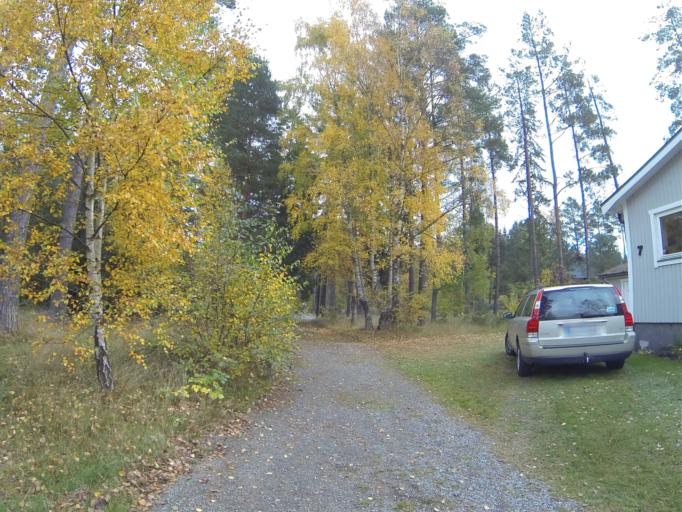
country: SE
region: Skane
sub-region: Sjobo Kommun
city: Sjoebo
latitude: 55.6335
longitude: 13.6542
